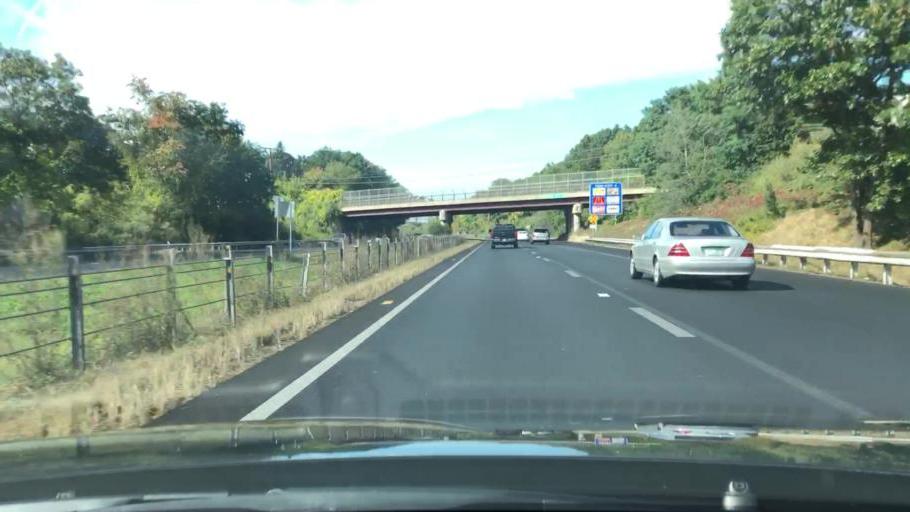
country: US
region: Massachusetts
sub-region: Essex County
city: Lawrence
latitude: 42.7437
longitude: -71.1440
